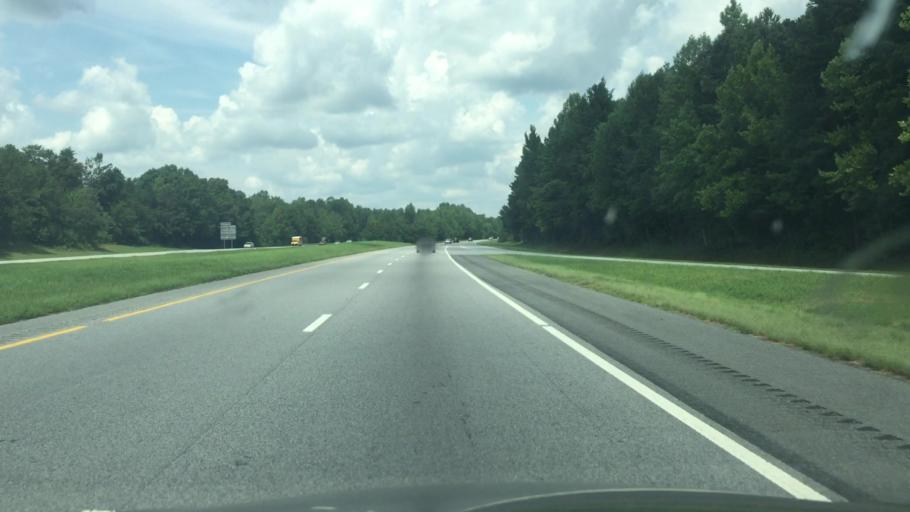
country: US
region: North Carolina
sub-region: Guilford County
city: Pleasant Garden
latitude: 35.9254
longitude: -79.8263
